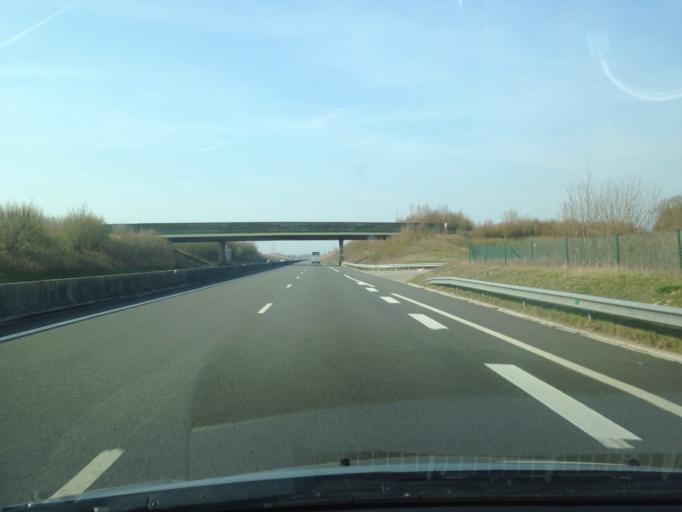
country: FR
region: Nord-Pas-de-Calais
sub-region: Departement du Pas-de-Calais
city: Verton
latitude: 50.3826
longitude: 1.6971
